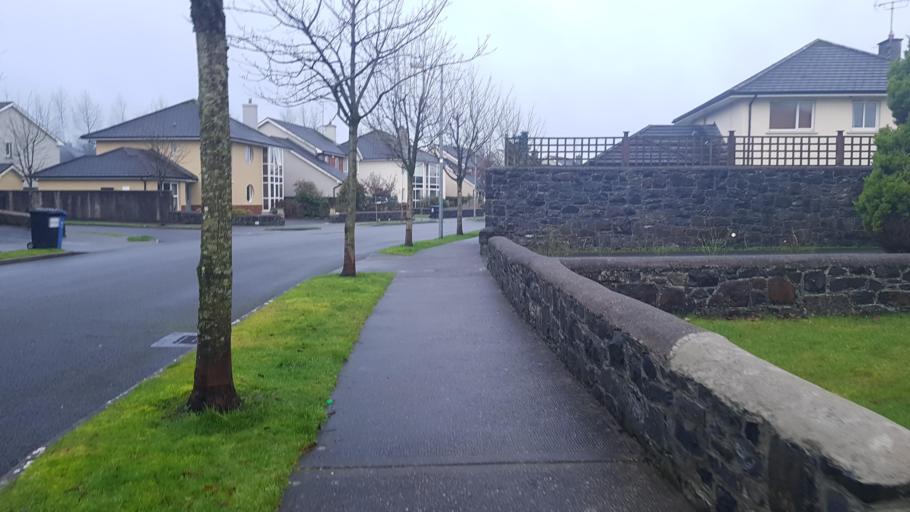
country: IE
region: Connaught
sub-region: County Galway
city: Tuam
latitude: 53.5232
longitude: -8.8483
